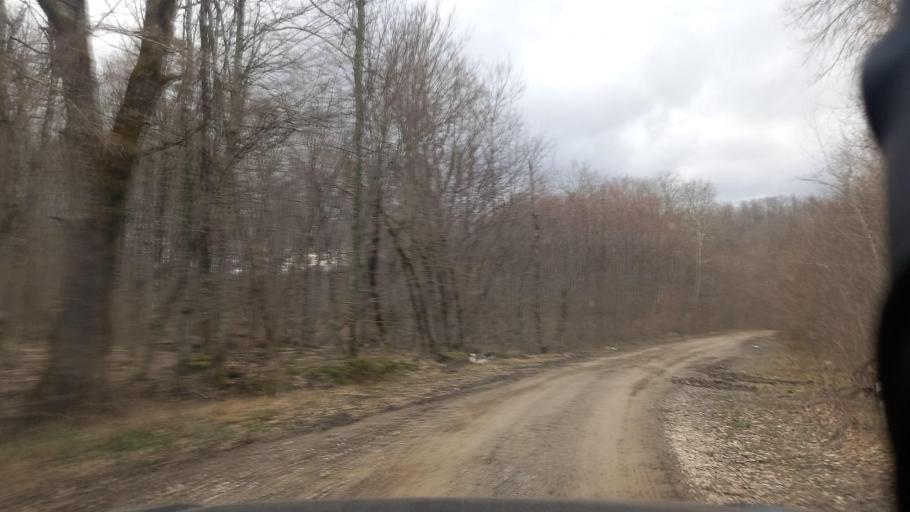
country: RU
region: Krasnodarskiy
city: Dzhubga
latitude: 44.4857
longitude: 38.7742
